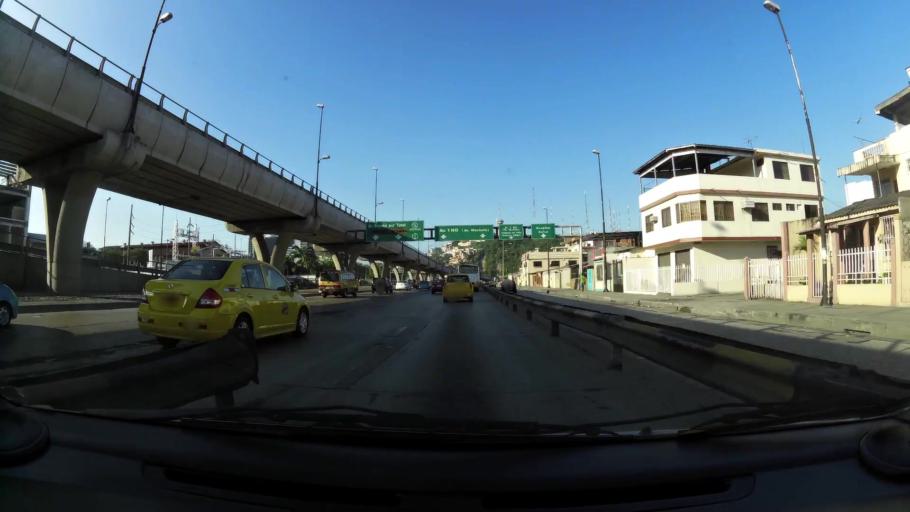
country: EC
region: Guayas
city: Eloy Alfaro
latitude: -2.1720
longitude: -79.8797
